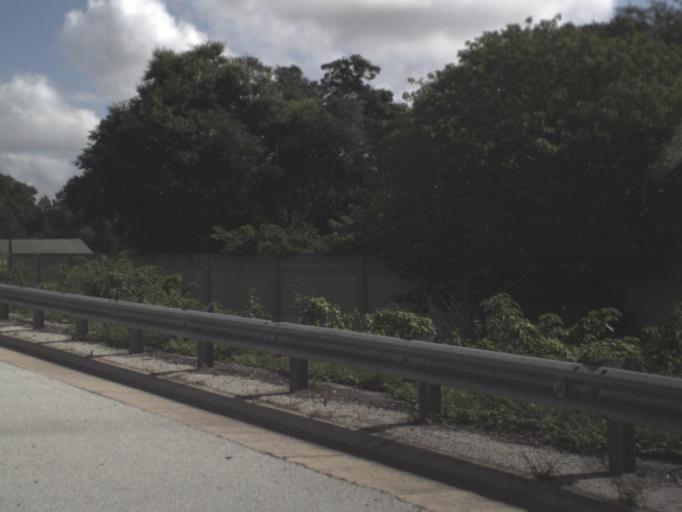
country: US
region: Florida
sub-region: Hillsborough County
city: University
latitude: 28.0612
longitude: -82.4546
